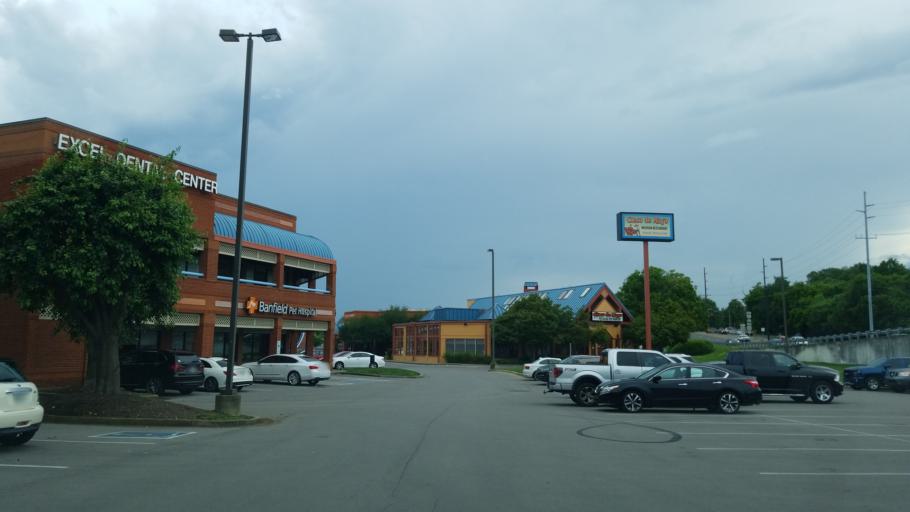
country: US
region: Tennessee
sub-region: Williamson County
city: Brentwood
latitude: 36.0369
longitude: -86.7879
